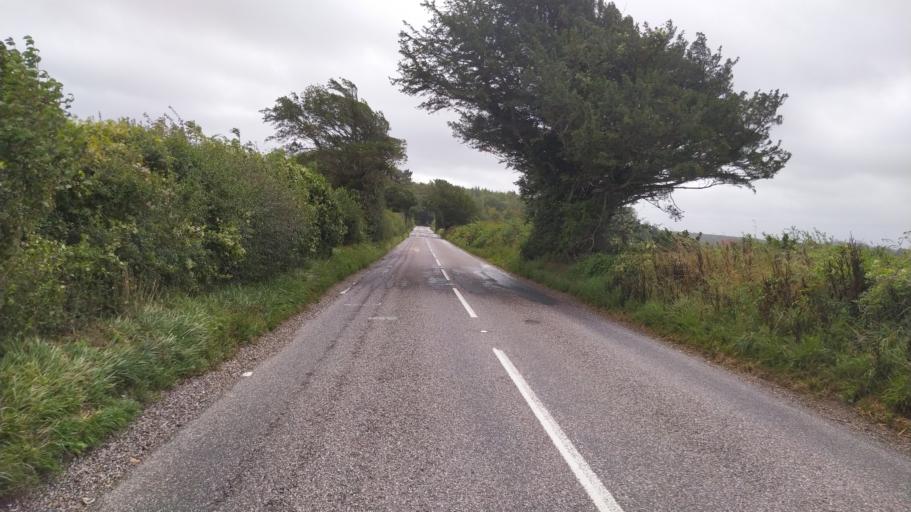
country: GB
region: England
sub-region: Wiltshire
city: Bower Chalke
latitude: 50.9204
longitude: -1.9444
